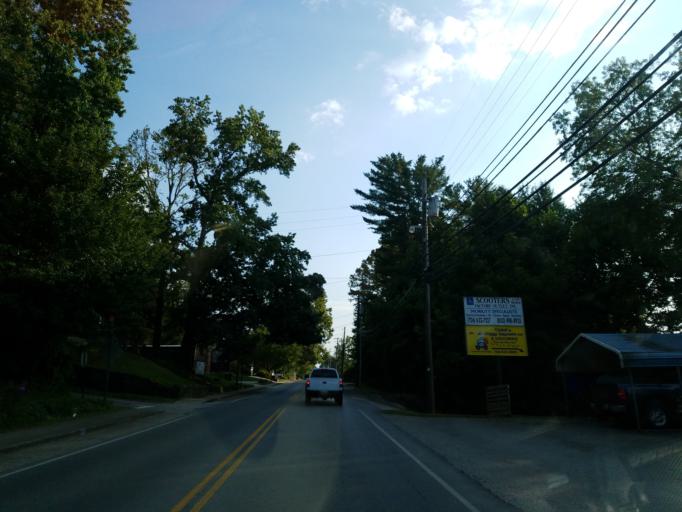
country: US
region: Georgia
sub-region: Fannin County
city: Blue Ridge
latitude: 34.8663
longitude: -84.3225
